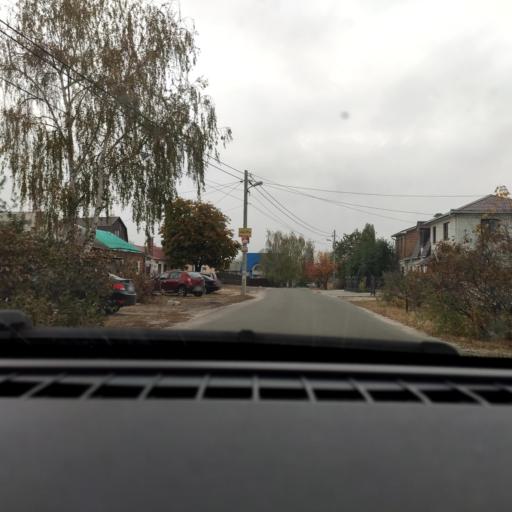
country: RU
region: Voronezj
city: Voronezh
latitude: 51.7040
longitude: 39.2695
